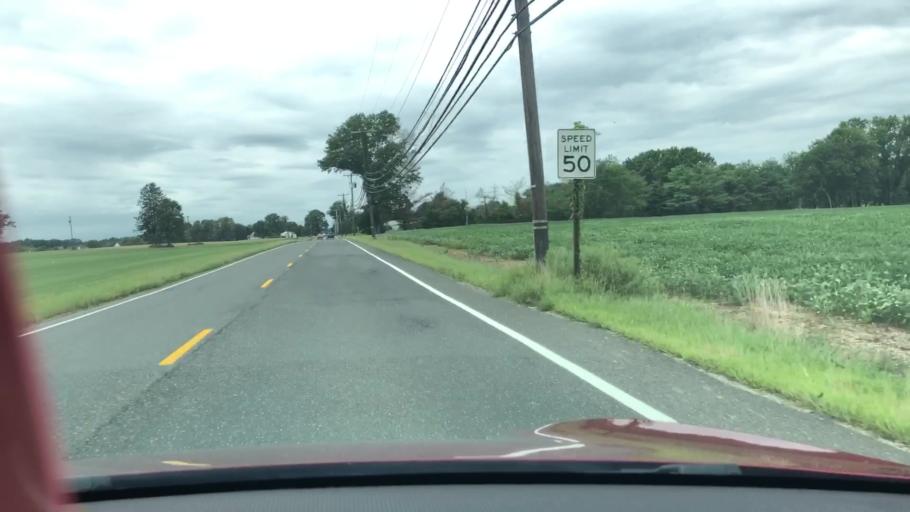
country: US
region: New Jersey
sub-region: Monmouth County
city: Shrewsbury
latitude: 40.1734
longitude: -74.5540
